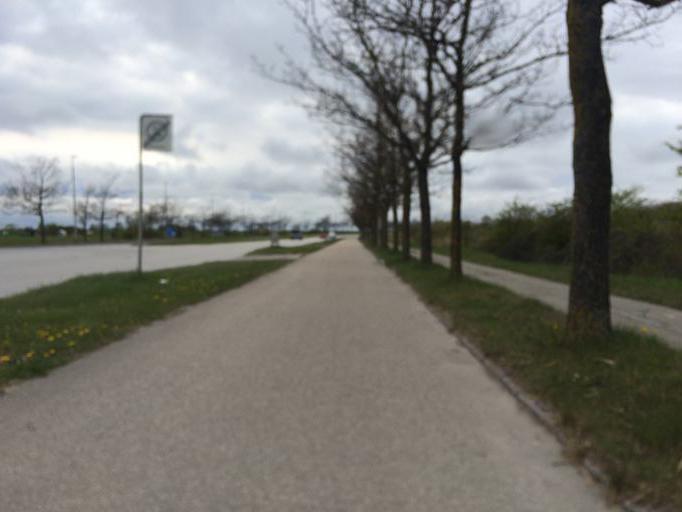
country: DK
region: Capital Region
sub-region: Hvidovre Kommune
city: Hvidovre
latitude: 55.6137
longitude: 12.4503
